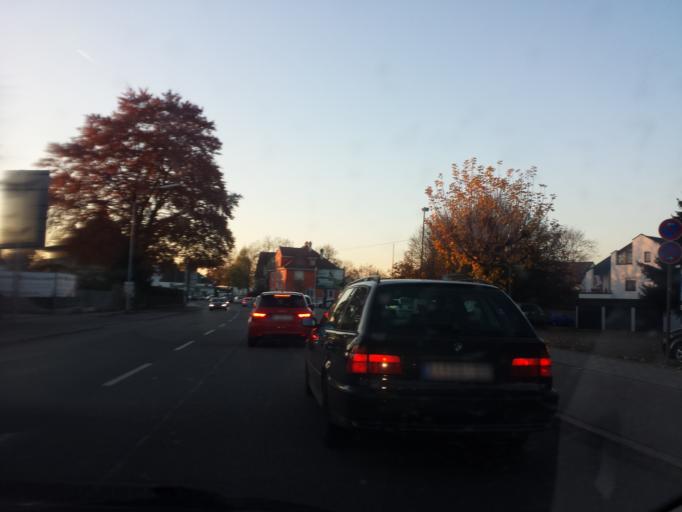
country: DE
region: Bavaria
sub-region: Upper Bavaria
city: Ingolstadt
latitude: 48.7682
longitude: 11.4102
